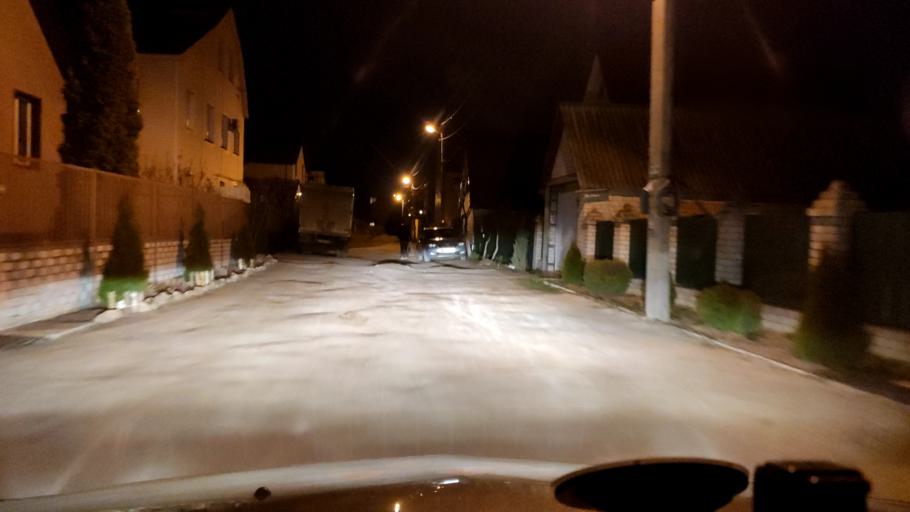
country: RU
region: Voronezj
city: Pridonskoy
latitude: 51.6177
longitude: 39.0572
